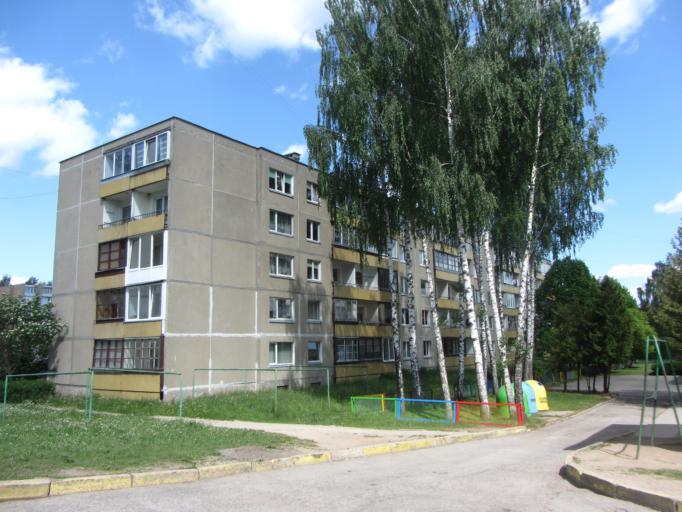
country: LT
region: Utenos apskritis
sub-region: Utena
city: Utena
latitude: 55.5052
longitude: 25.5862
